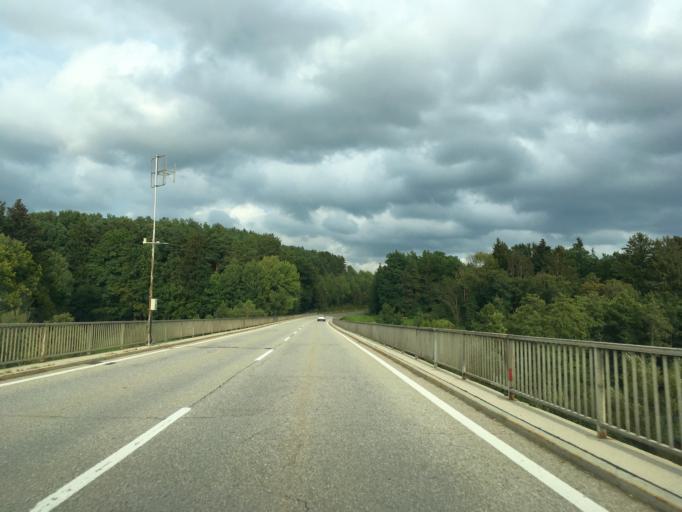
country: AT
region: Styria
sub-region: Politischer Bezirk Hartberg-Fuerstenfeld
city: Dechantskirchen
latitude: 47.4156
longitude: 16.0263
